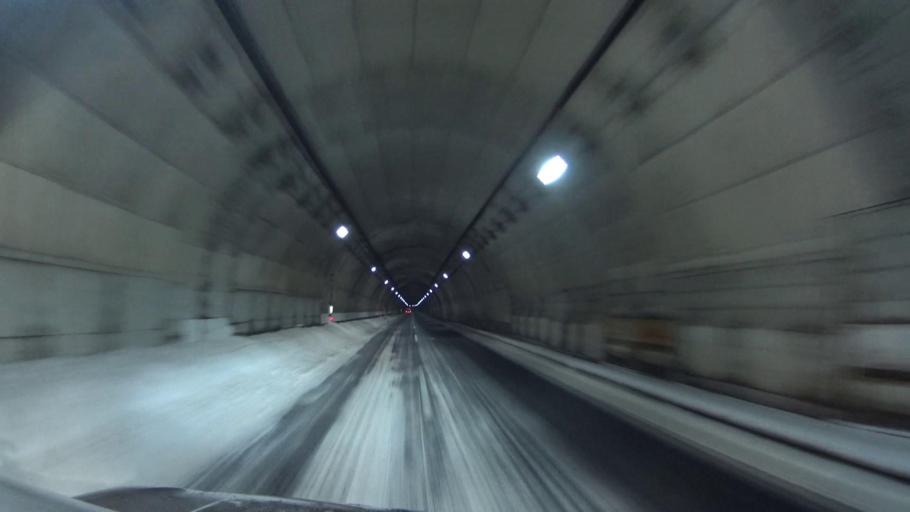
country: JP
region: Hokkaido
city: Otaru
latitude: 43.1661
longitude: 141.0932
